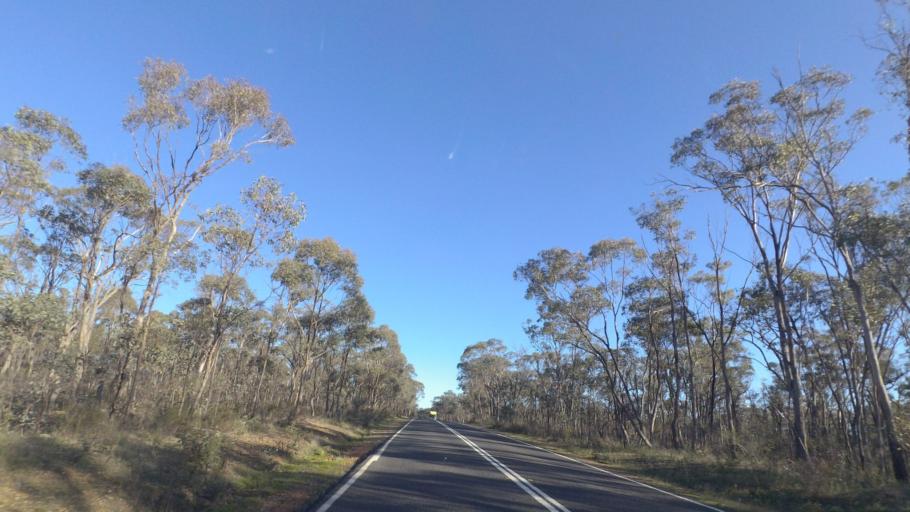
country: AU
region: Victoria
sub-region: Greater Bendigo
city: Kennington
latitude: -36.9056
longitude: 144.4944
